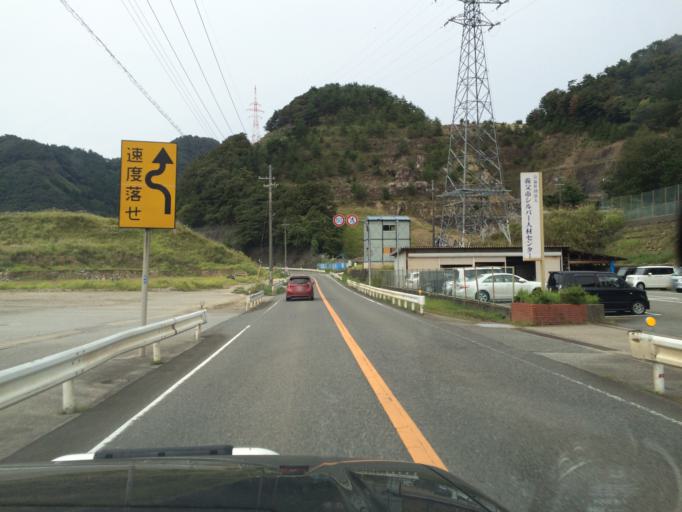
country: JP
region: Hyogo
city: Toyooka
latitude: 35.4048
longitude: 134.7831
